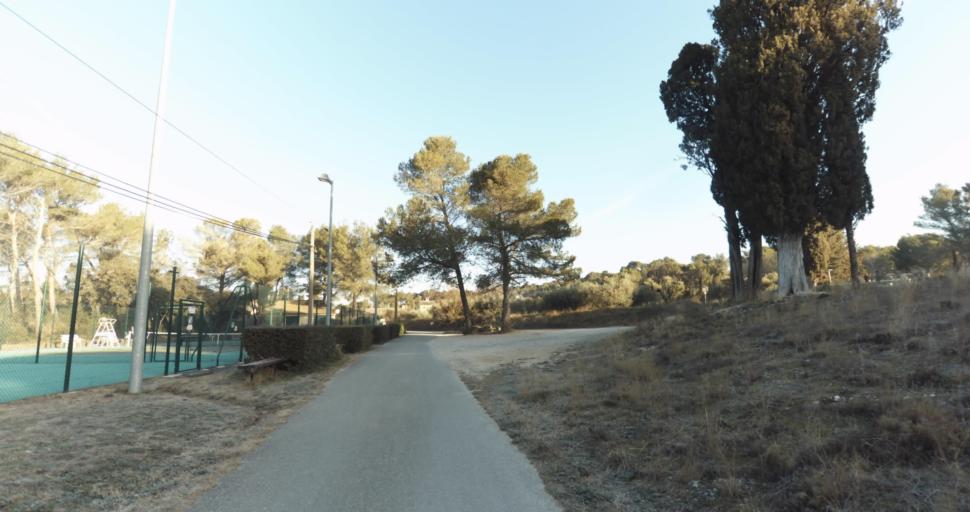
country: FR
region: Provence-Alpes-Cote d'Azur
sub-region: Departement des Bouches-du-Rhone
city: Barbentane
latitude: 43.8930
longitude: 4.7463
